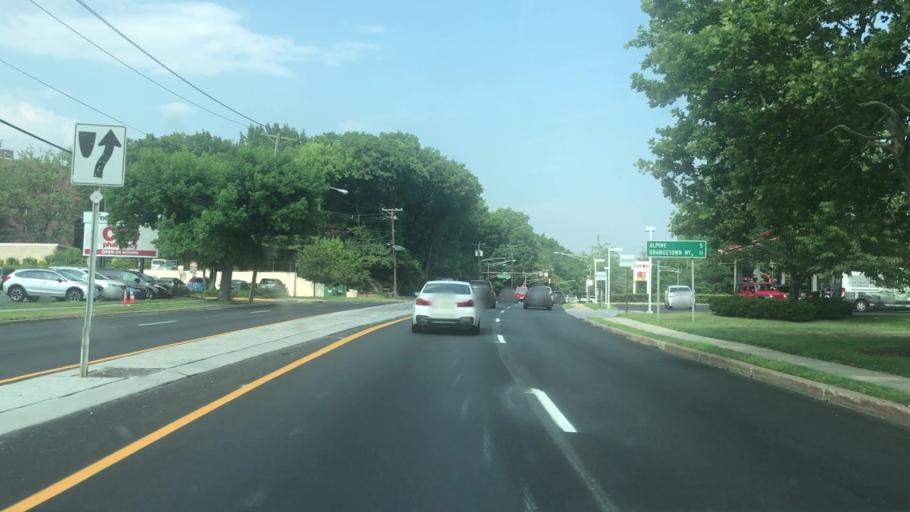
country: US
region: New Jersey
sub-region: Bergen County
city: Fort Lee
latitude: 40.8607
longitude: -73.9698
